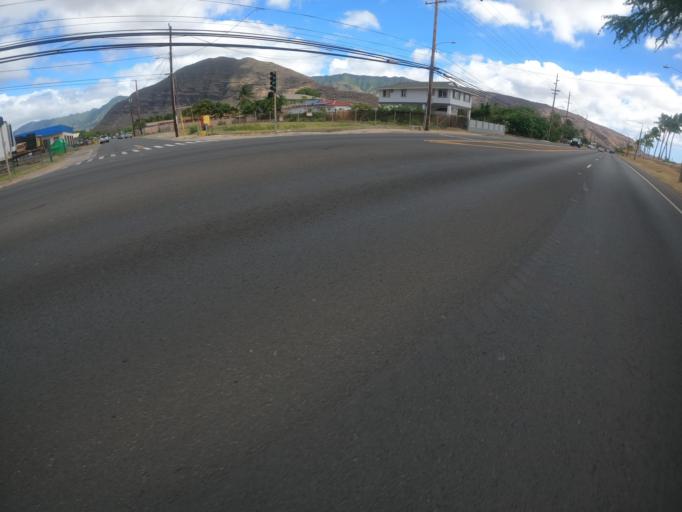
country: US
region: Hawaii
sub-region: Honolulu County
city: Nanakuli
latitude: 21.3916
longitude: -158.1564
